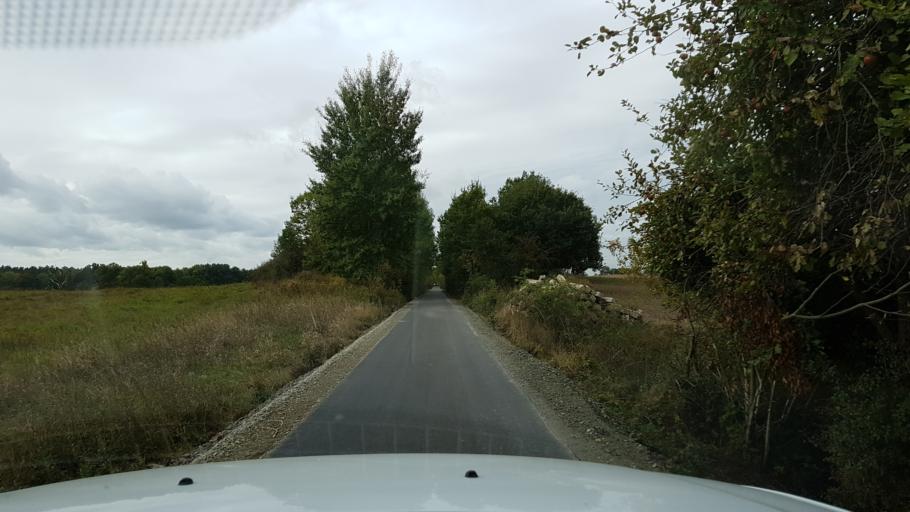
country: PL
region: West Pomeranian Voivodeship
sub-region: Powiat gryfinski
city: Moryn
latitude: 52.8878
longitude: 14.4424
